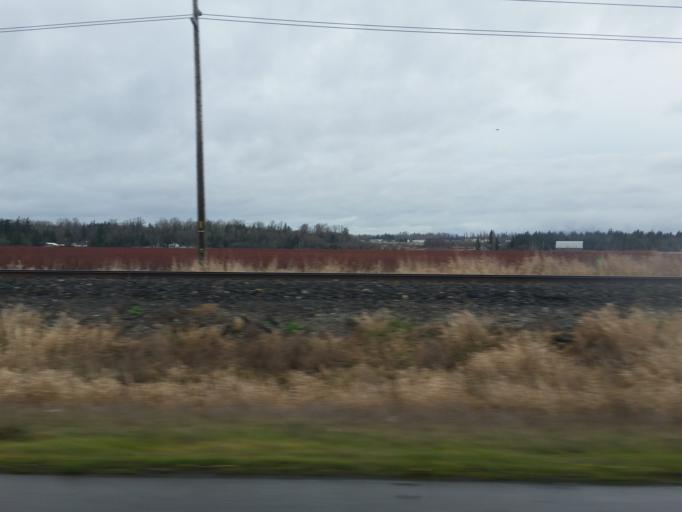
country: US
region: Washington
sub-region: Skagit County
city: Mount Vernon
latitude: 48.4526
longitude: -122.4027
